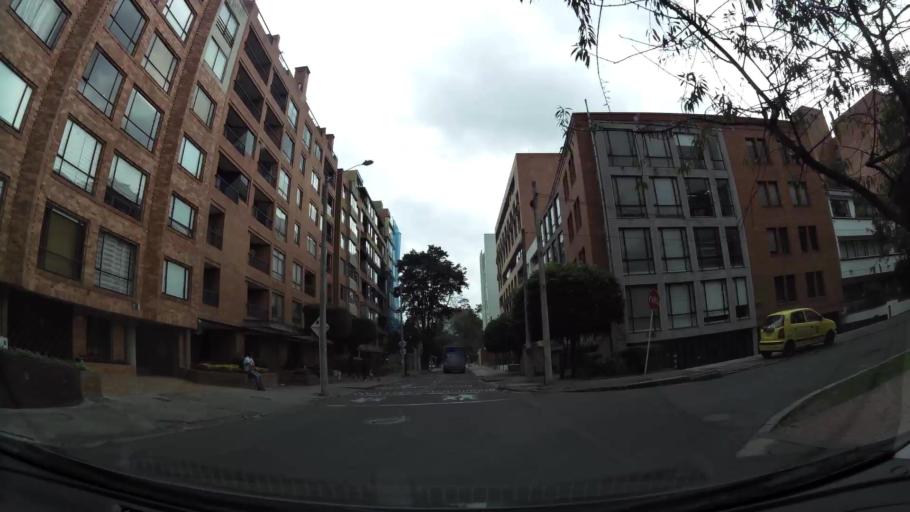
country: CO
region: Bogota D.C.
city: Barrio San Luis
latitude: 4.6722
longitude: -74.0563
